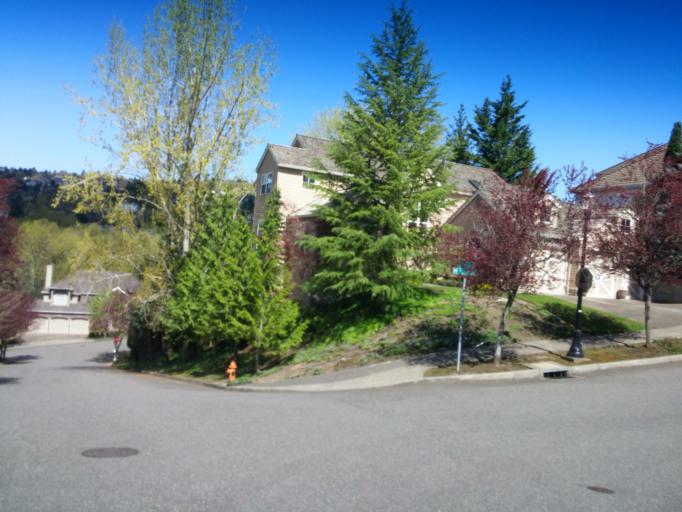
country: US
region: Oregon
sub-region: Washington County
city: West Haven
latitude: 45.5343
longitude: -122.7778
